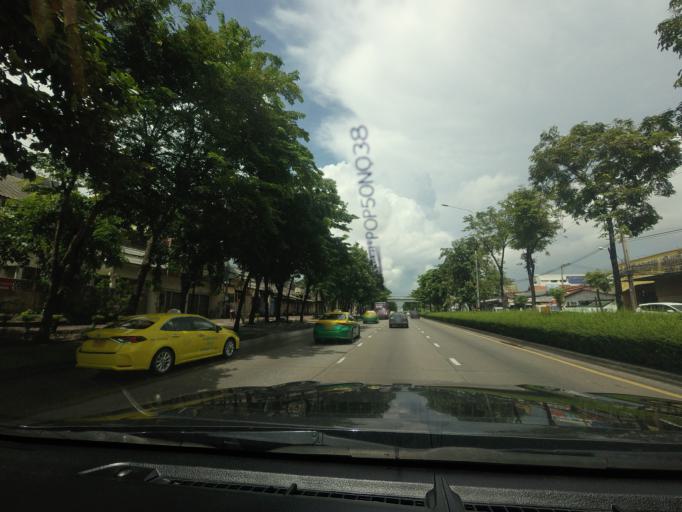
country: TH
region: Bangkok
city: Bang Khae
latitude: 13.7084
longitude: 100.3816
